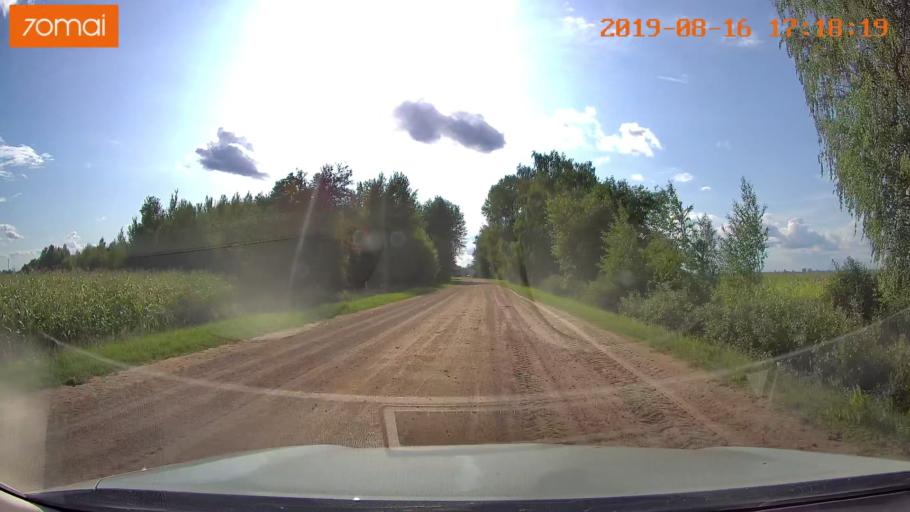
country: BY
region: Mogilev
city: Hlusha
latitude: 53.1698
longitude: 28.7911
